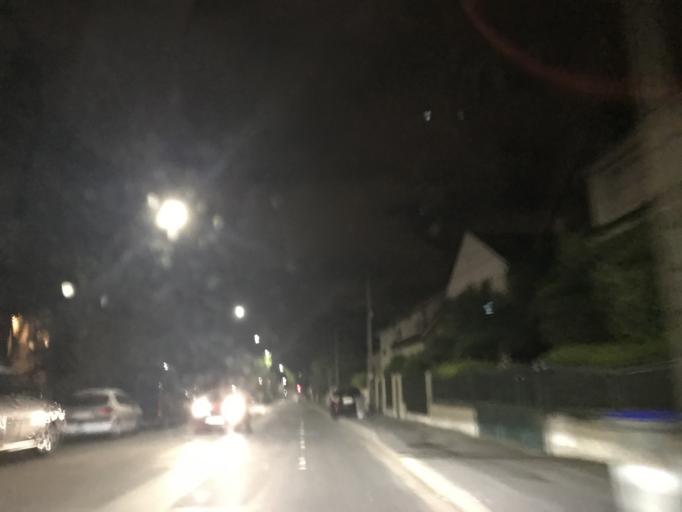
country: FR
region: Ile-de-France
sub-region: Departement des Yvelines
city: Sartrouville
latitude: 48.9458
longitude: 2.1990
